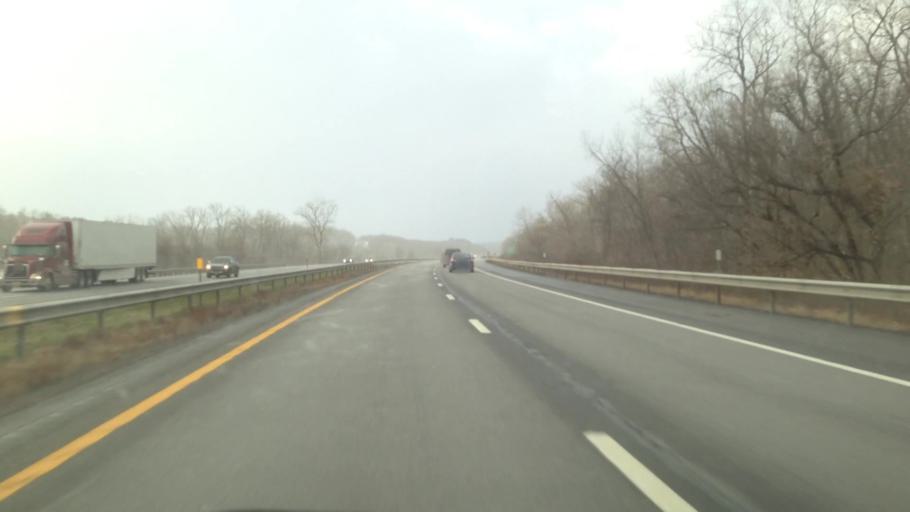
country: US
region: New York
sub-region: Montgomery County
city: Tribes Hill
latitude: 42.9309
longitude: -74.3110
